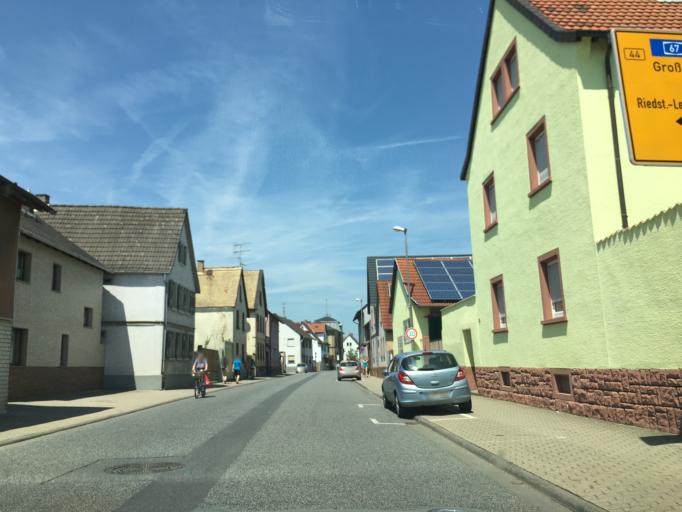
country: DE
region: Hesse
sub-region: Regierungsbezirk Darmstadt
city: Riedstadt
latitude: 49.8754
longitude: 8.4825
